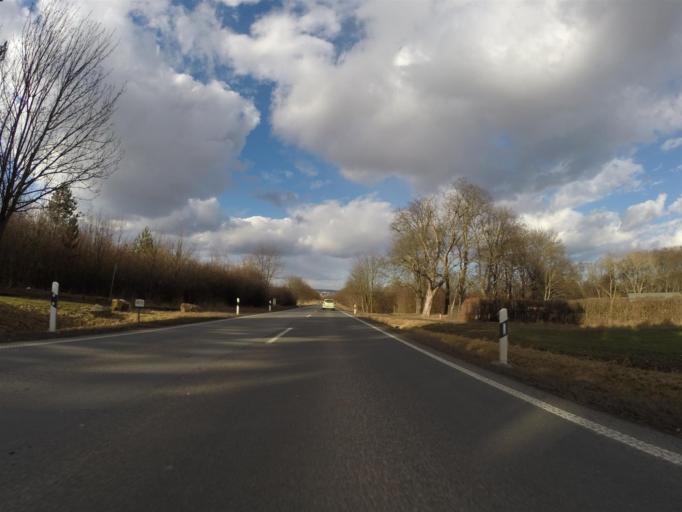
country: DE
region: Thuringia
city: Apolda
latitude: 51.0050
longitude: 11.5155
